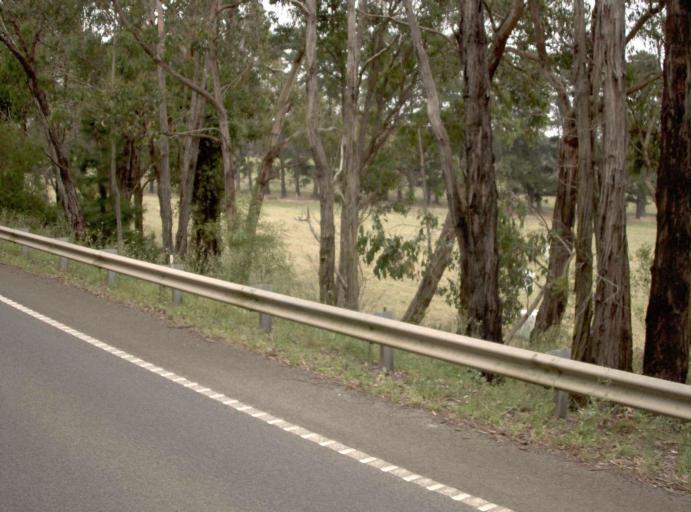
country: AU
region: Victoria
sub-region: Latrobe
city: Morwell
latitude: -38.2887
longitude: 146.3045
